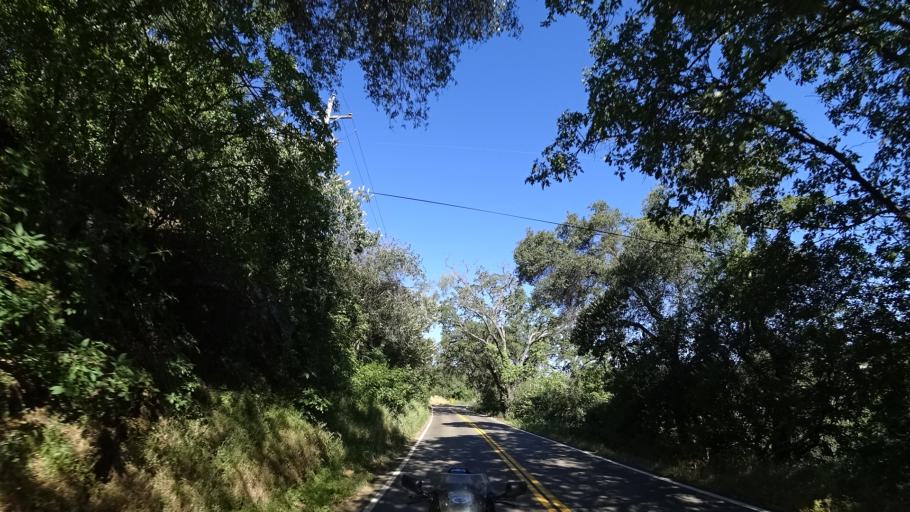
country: US
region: California
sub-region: Placer County
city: Newcastle
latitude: 38.8782
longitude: -121.1677
